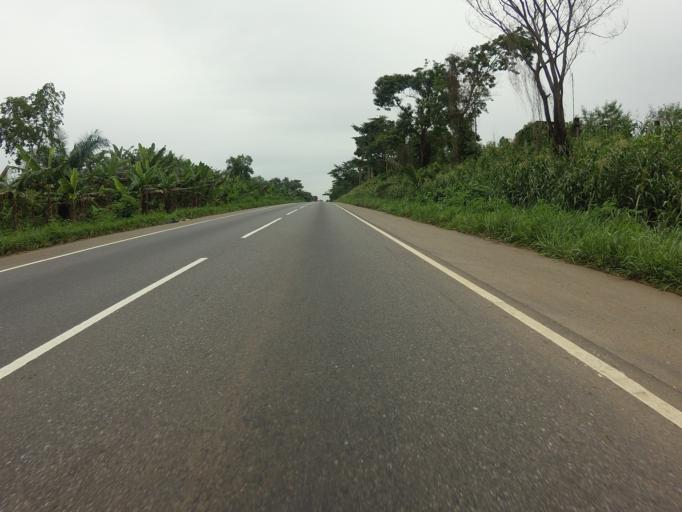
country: GH
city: Kibi
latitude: 6.1860
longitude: -0.4700
